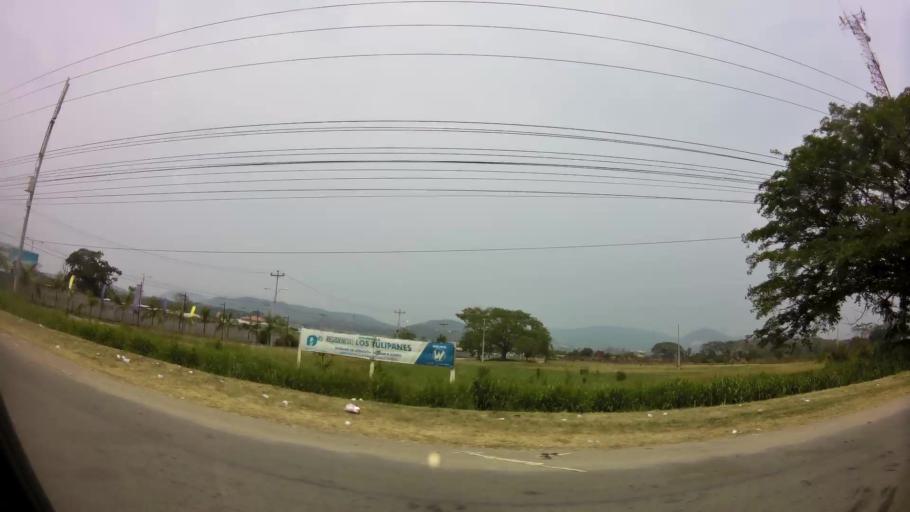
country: HN
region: Cortes
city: Villanueva
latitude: 15.3508
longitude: -87.9835
